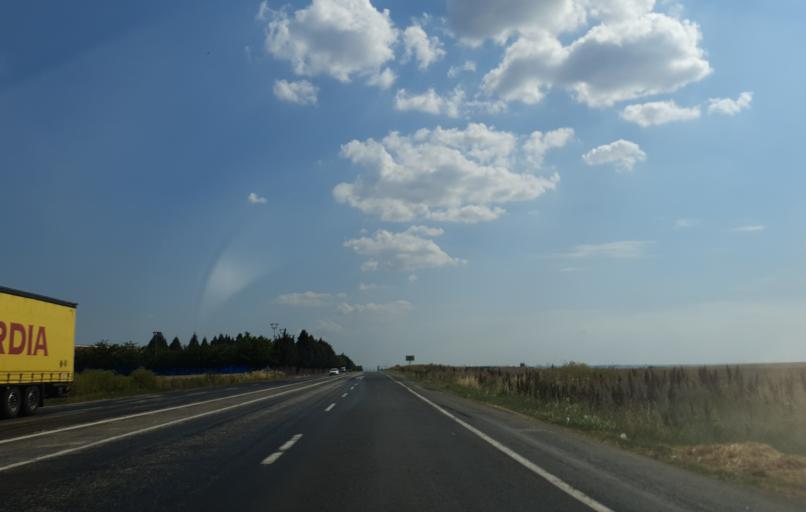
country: TR
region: Kirklareli
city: Buyukkaristiran
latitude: 41.2837
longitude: 27.5582
